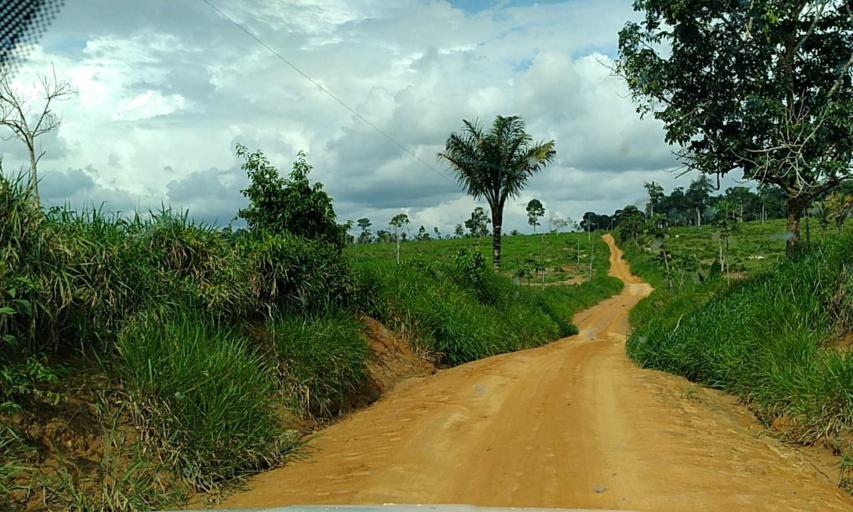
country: BR
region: Para
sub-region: Altamira
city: Altamira
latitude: -3.2354
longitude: -52.7408
